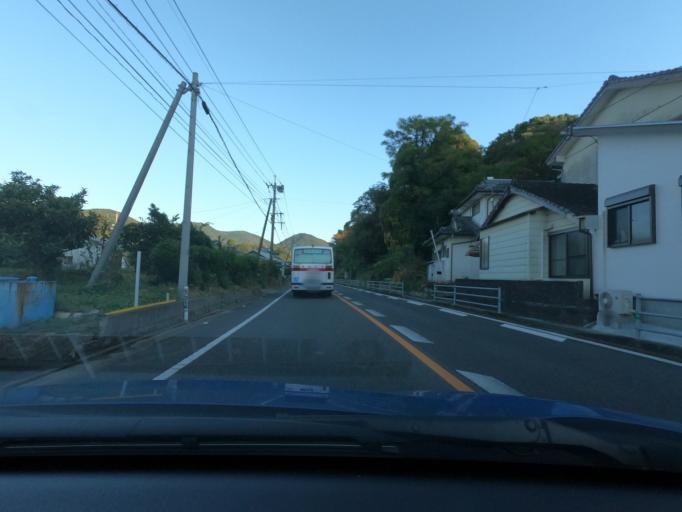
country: JP
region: Kagoshima
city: Akune
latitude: 31.9892
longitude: 130.1998
